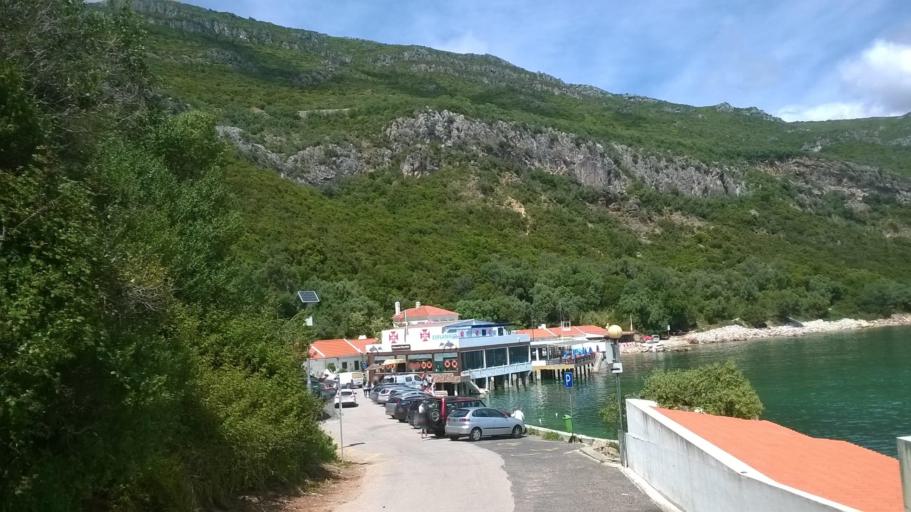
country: PT
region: Setubal
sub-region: Palmela
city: Quinta do Anjo
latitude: 38.4752
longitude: -8.9841
